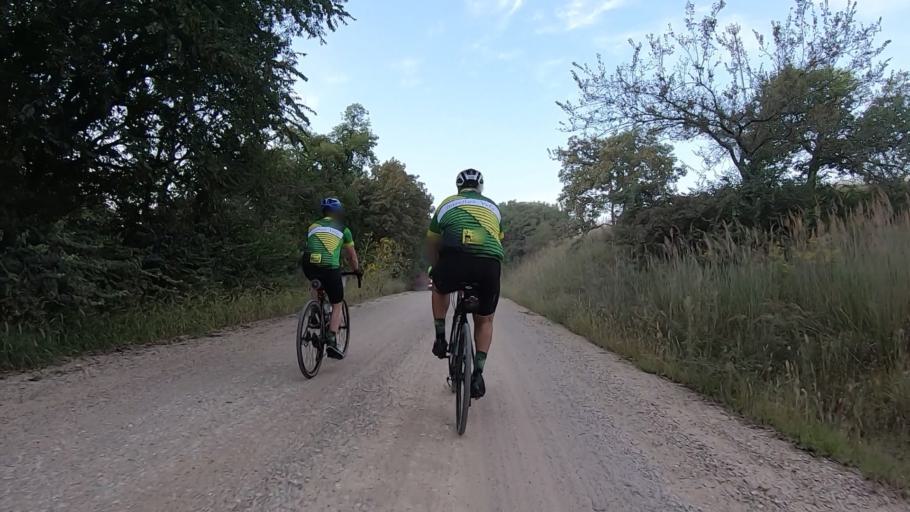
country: US
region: Kansas
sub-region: Marshall County
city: Marysville
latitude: 39.8375
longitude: -96.6653
